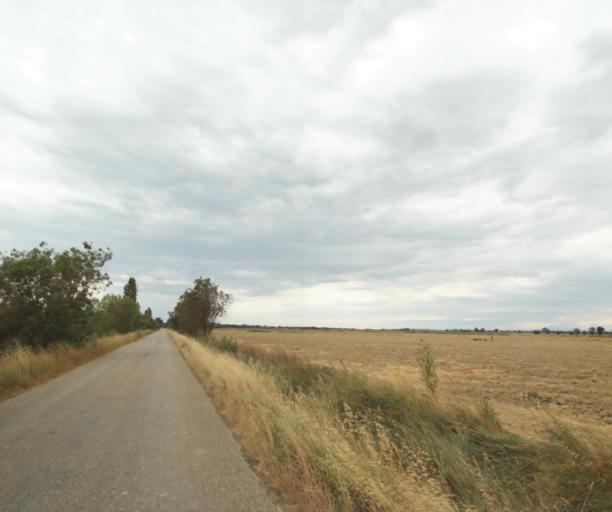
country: FR
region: Languedoc-Roussillon
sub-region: Departement de l'Herault
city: Saint-Just
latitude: 43.6093
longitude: 4.1377
